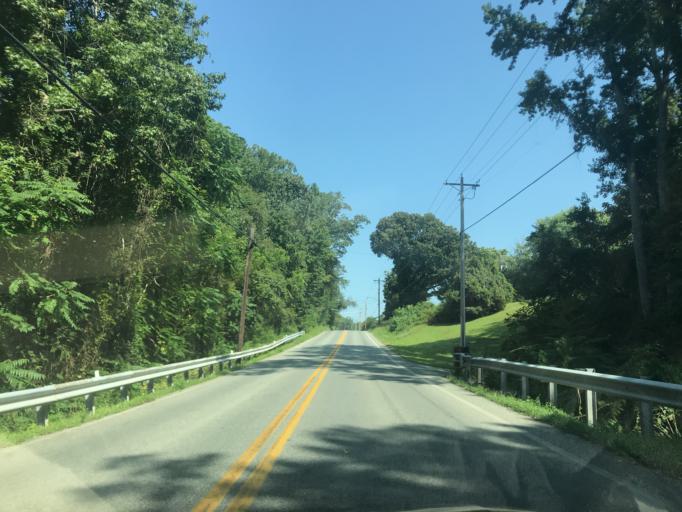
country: US
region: Maryland
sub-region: Calvert County
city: Prince Frederick
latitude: 38.4973
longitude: -76.6228
